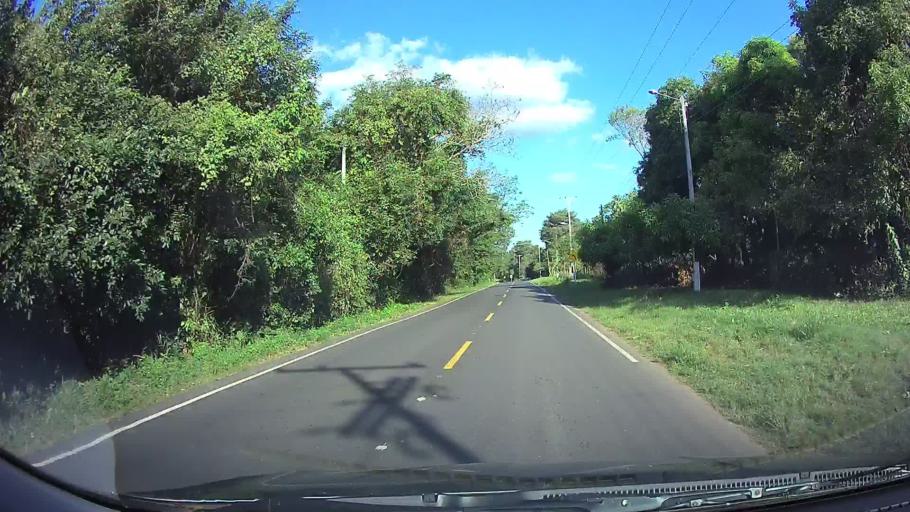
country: PY
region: Central
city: Aregua
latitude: -25.2905
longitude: -57.3943
